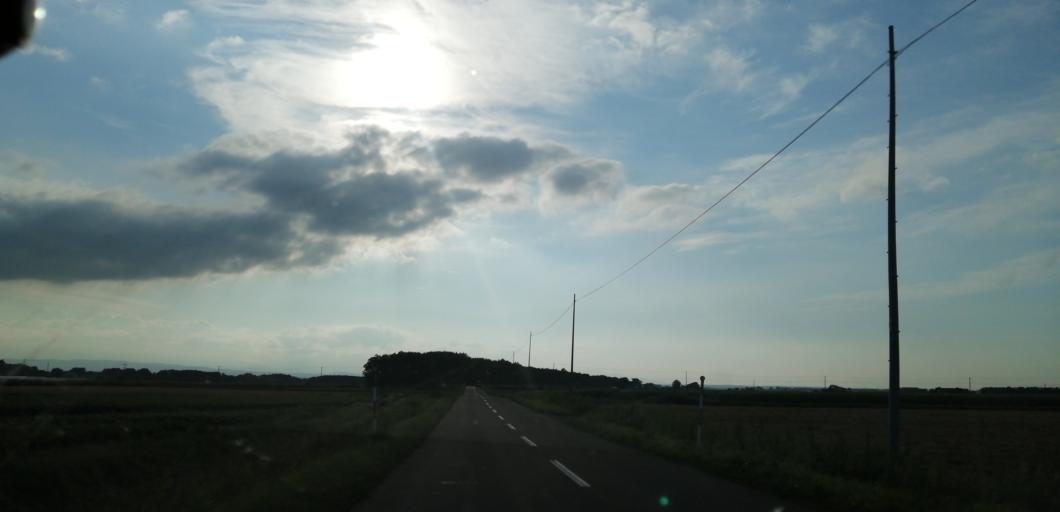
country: JP
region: Hokkaido
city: Chitose
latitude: 42.9366
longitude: 141.7098
